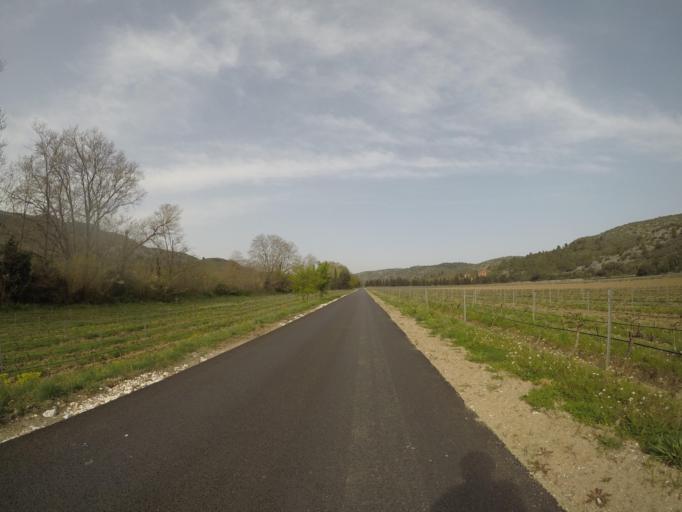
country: FR
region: Languedoc-Roussillon
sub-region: Departement des Pyrenees-Orientales
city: Estagel
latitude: 42.7756
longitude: 2.7444
